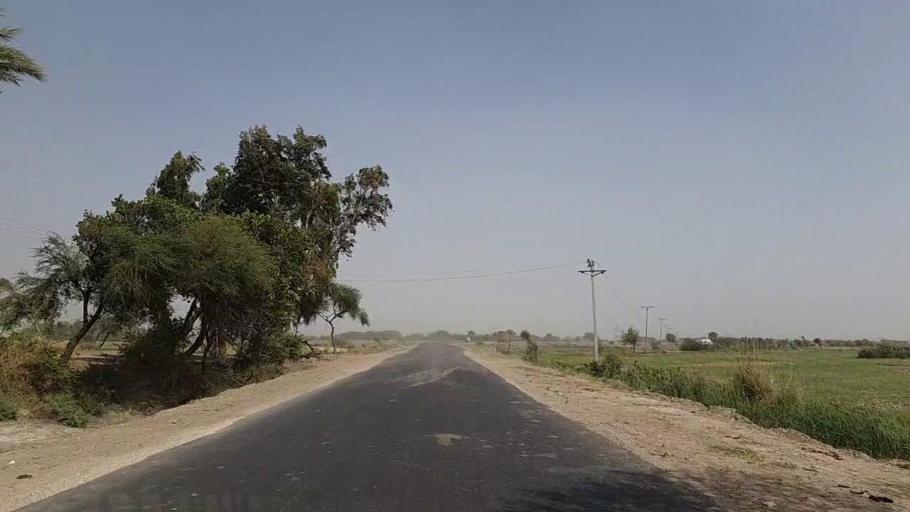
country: PK
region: Sindh
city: Tando Bago
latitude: 24.8095
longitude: 68.9259
